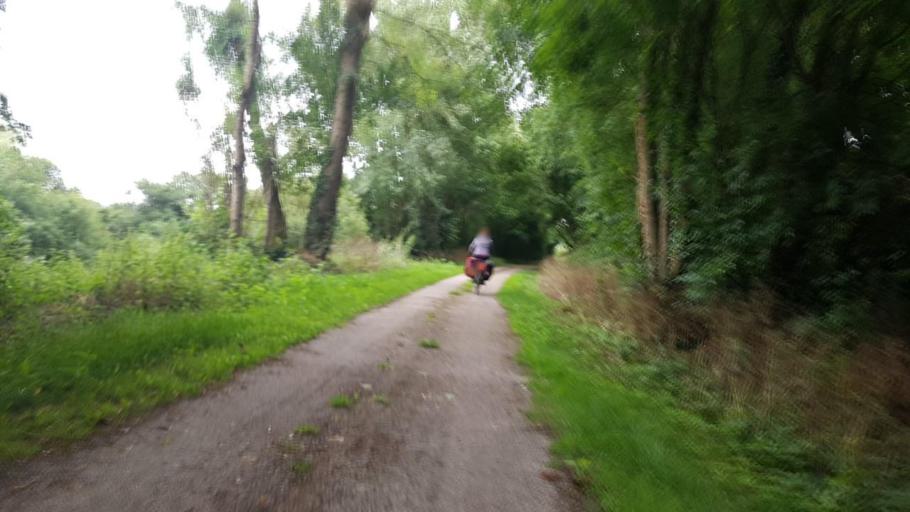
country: FR
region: Picardie
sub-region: Departement de l'Aisne
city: Buironfosse
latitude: 49.9056
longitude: 3.8586
